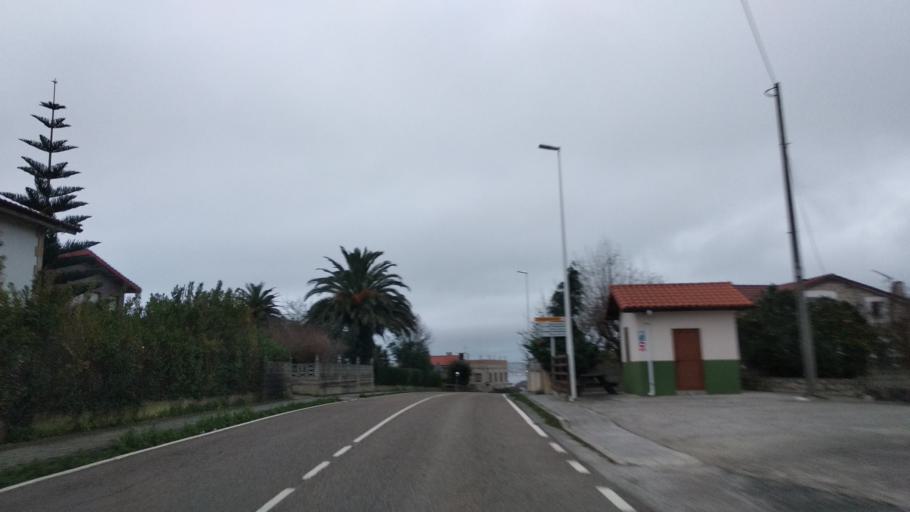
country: ES
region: Cantabria
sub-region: Provincia de Cantabria
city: Santander
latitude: 43.4517
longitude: -3.7380
